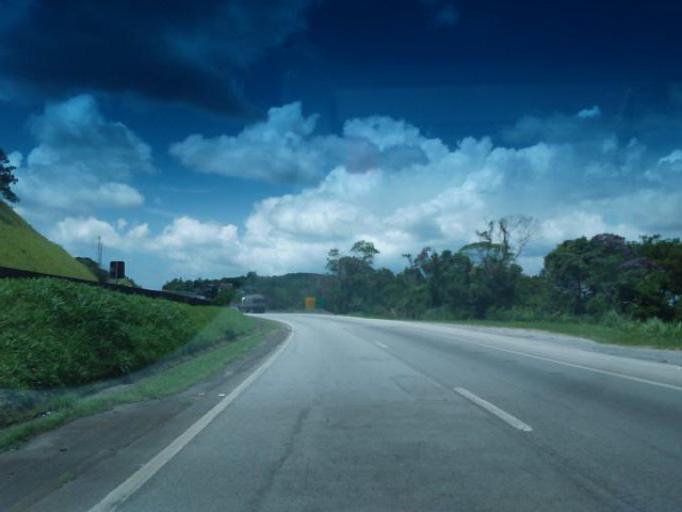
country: BR
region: Sao Paulo
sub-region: Juquitiba
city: Juquitiba
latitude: -23.9767
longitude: -47.1439
